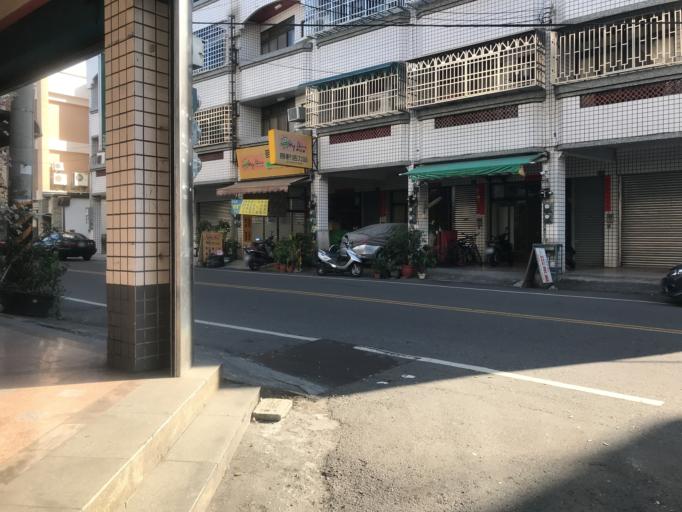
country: TW
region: Taiwan
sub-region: Nantou
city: Nantou
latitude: 23.8544
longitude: 120.5846
